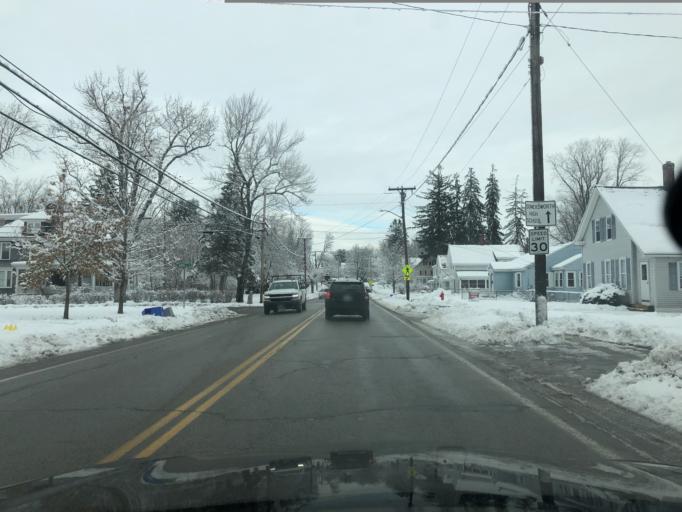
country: US
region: New Hampshire
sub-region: Strafford County
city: Somersworth
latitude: 43.2493
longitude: -70.8728
